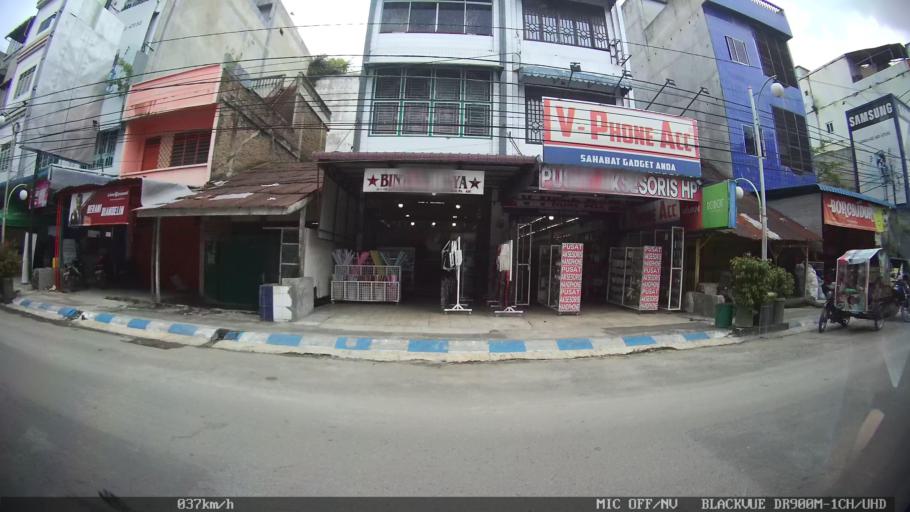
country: ID
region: North Sumatra
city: Percut
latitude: 3.5613
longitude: 98.8752
